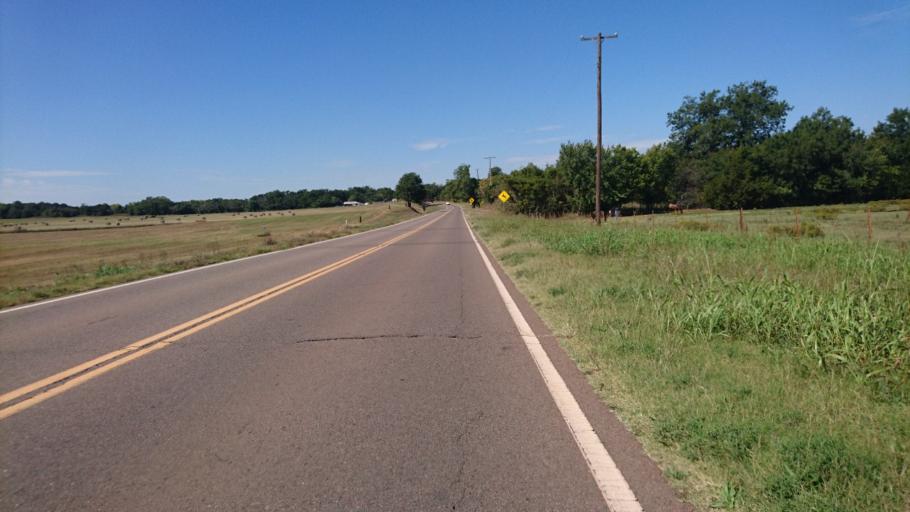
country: US
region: Oklahoma
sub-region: Oklahoma County
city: Luther
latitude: 35.6670
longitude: -97.2411
